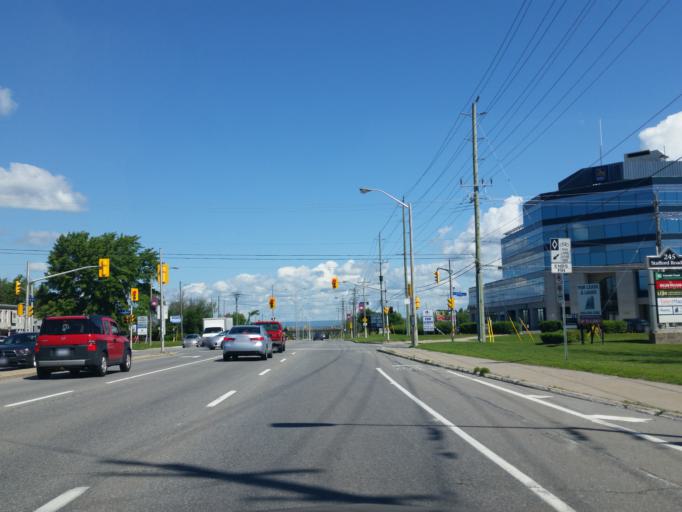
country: CA
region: Ontario
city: Bells Corners
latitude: 45.3248
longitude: -75.8348
